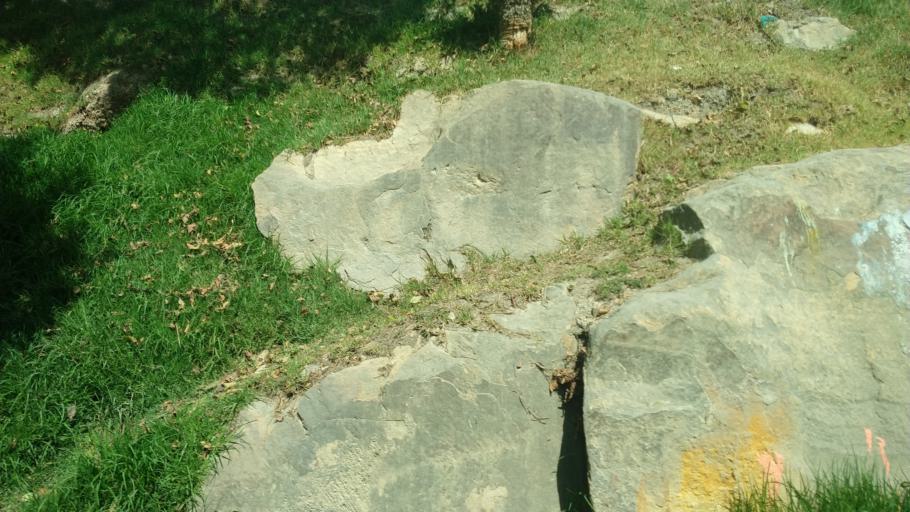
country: CO
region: Cundinamarca
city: Soacha
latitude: 4.5649
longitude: -74.1871
